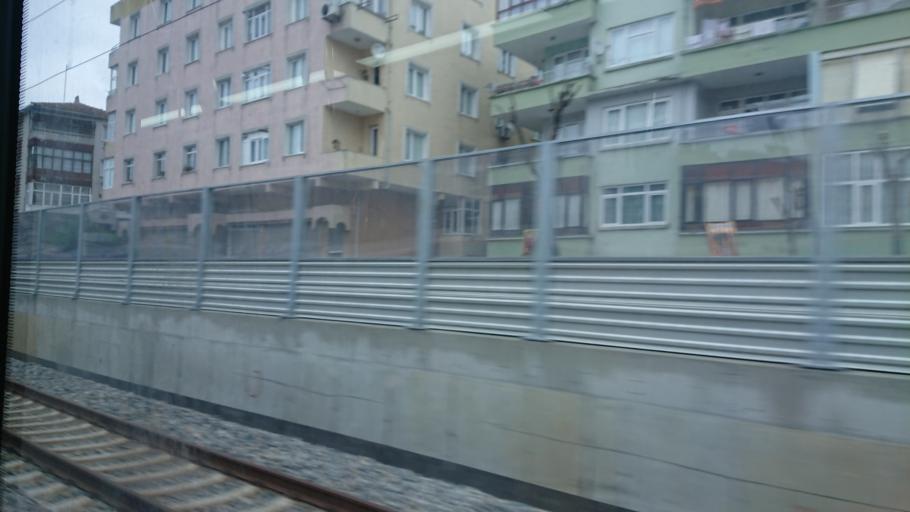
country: TR
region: Istanbul
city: Mahmutbey
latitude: 40.9980
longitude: 28.7675
